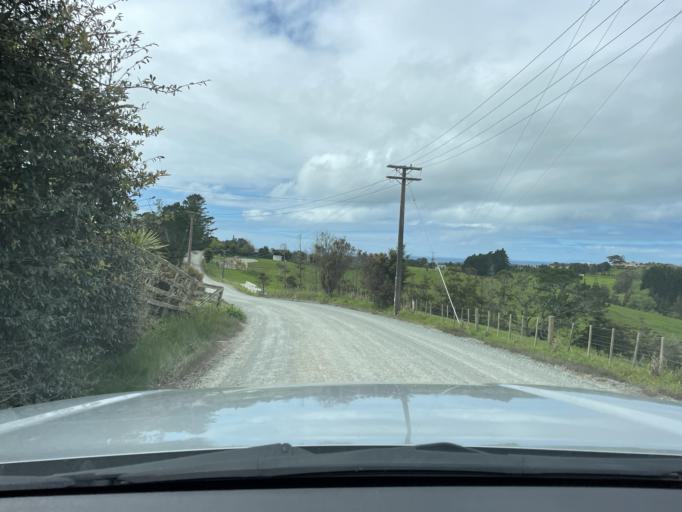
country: NZ
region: Auckland
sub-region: Auckland
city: Wellsford
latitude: -36.1724
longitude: 174.5777
